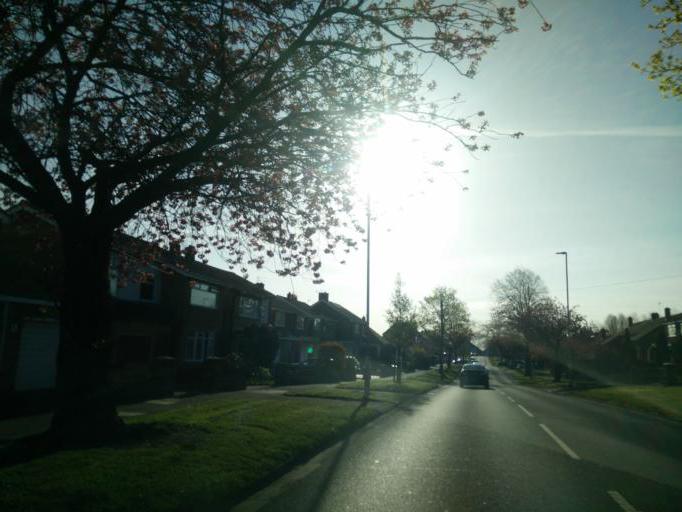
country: GB
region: England
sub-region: Stockton-on-Tees
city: Billingham
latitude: 54.6095
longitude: -1.3049
